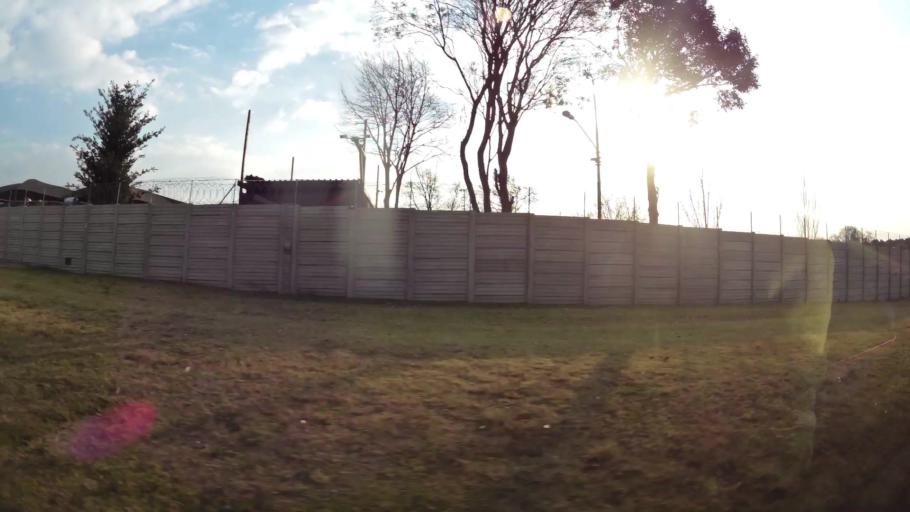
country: ZA
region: Gauteng
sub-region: Ekurhuleni Metropolitan Municipality
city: Benoni
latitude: -26.1242
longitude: 28.3039
